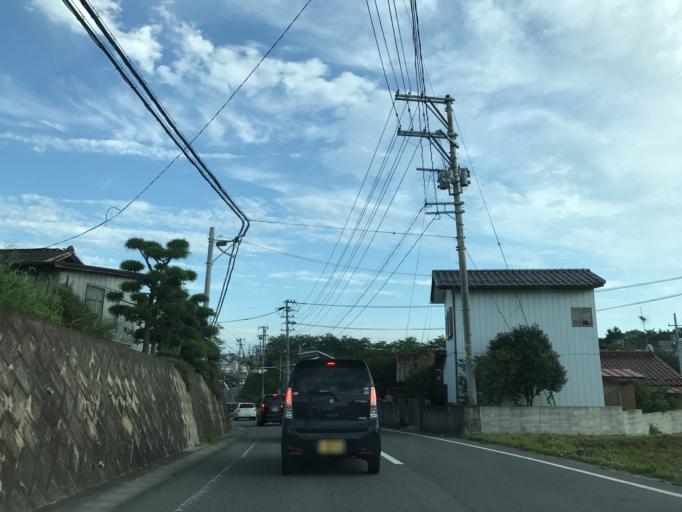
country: JP
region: Fukushima
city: Sukagawa
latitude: 37.3129
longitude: 140.3600
